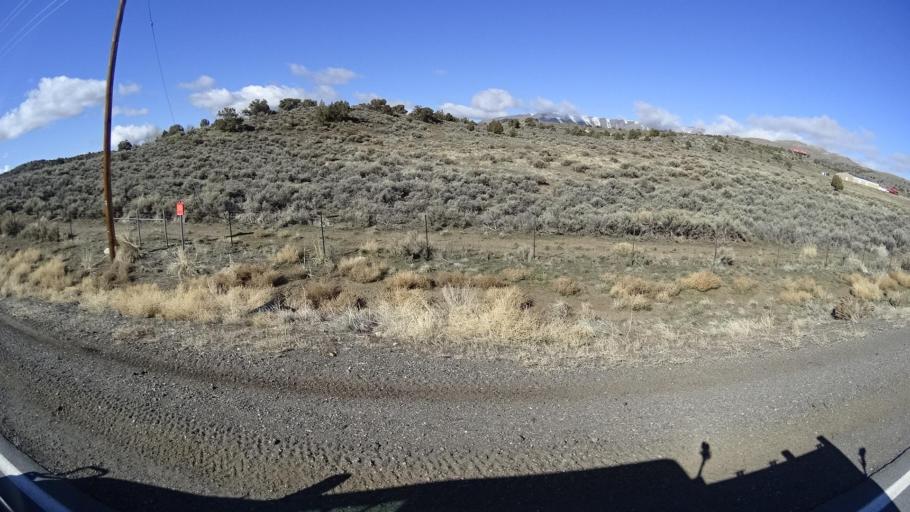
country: US
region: Nevada
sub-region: Washoe County
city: Cold Springs
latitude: 39.7467
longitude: -119.8859
